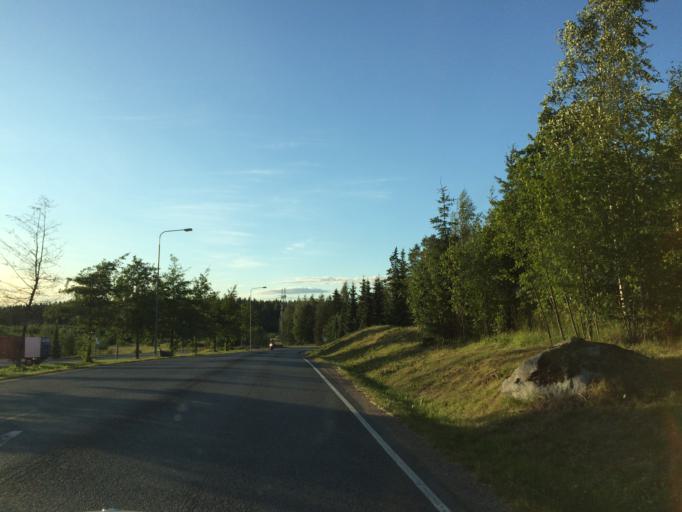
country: FI
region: Haeme
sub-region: Riihimaeki
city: Riihimaeki
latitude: 60.7516
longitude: 24.7380
